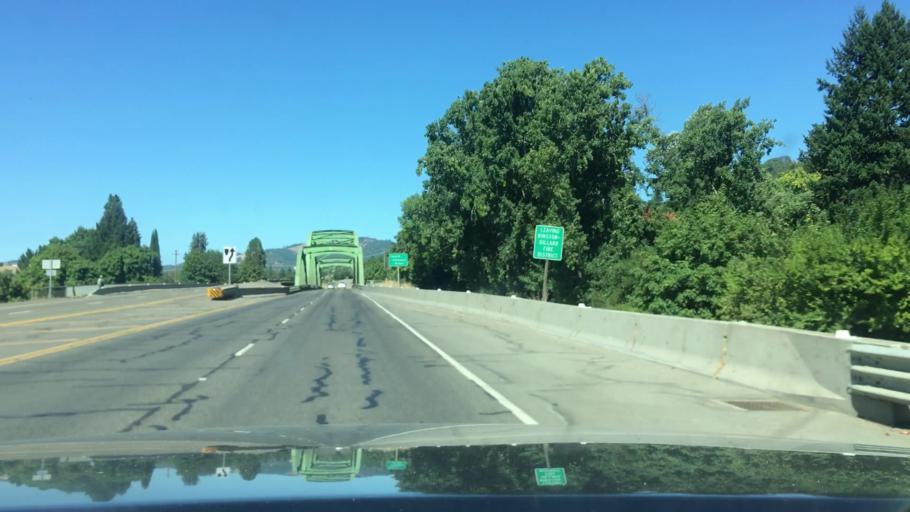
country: US
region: Oregon
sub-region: Douglas County
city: Winston
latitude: 43.1328
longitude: -123.4007
